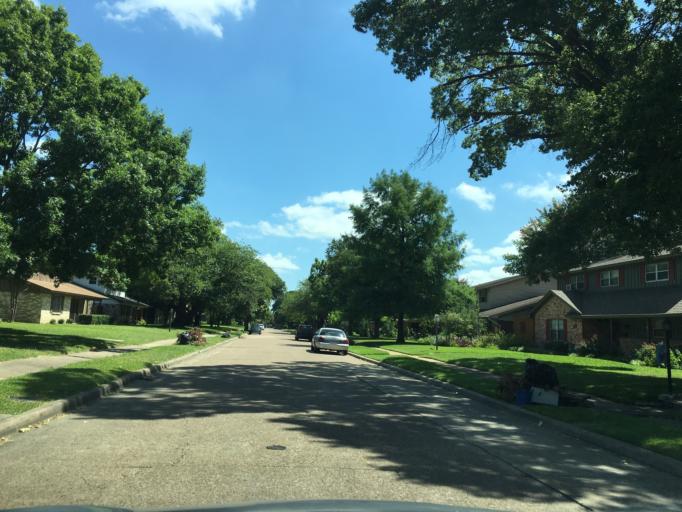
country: US
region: Texas
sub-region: Dallas County
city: Garland
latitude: 32.8476
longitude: -96.6563
